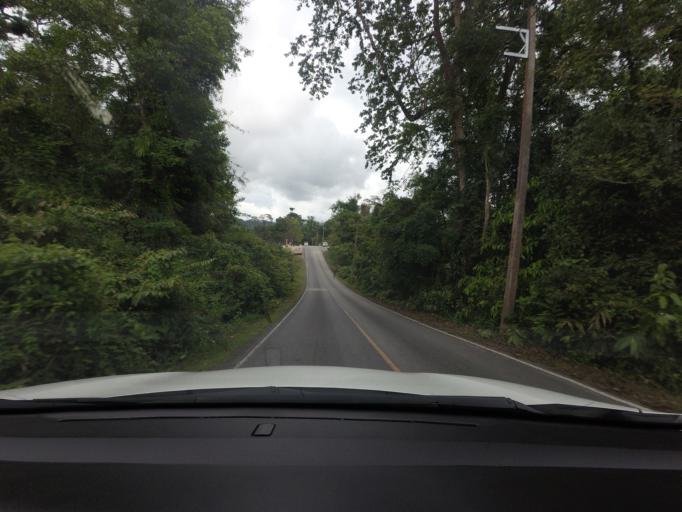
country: TH
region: Nakhon Ratchasima
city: Pak Chong
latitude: 14.4740
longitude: 101.3890
